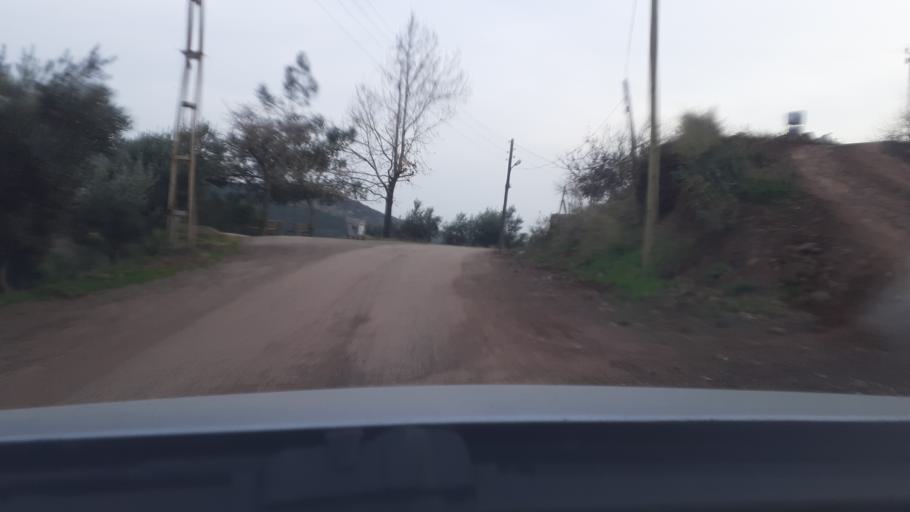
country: TR
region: Hatay
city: Kirikhan
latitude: 36.5345
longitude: 36.3144
